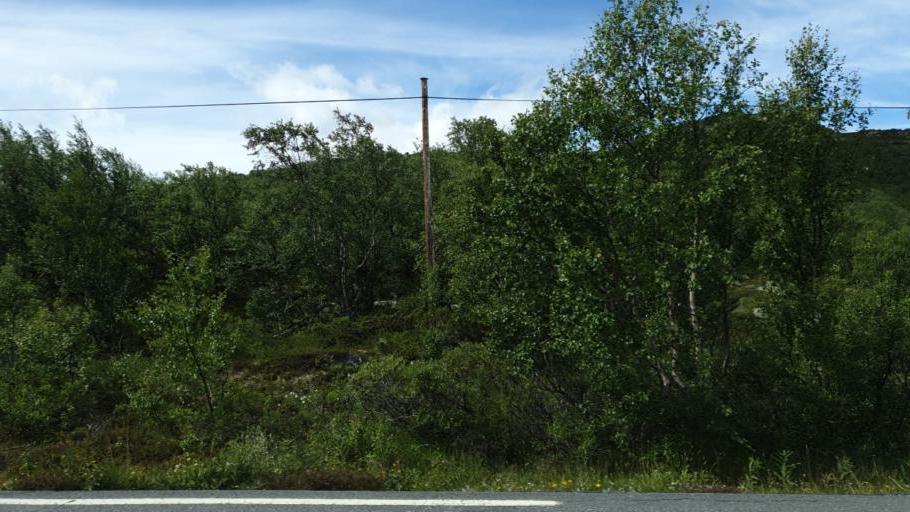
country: NO
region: Oppland
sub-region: Oystre Slidre
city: Heggenes
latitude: 61.4993
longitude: 8.8433
